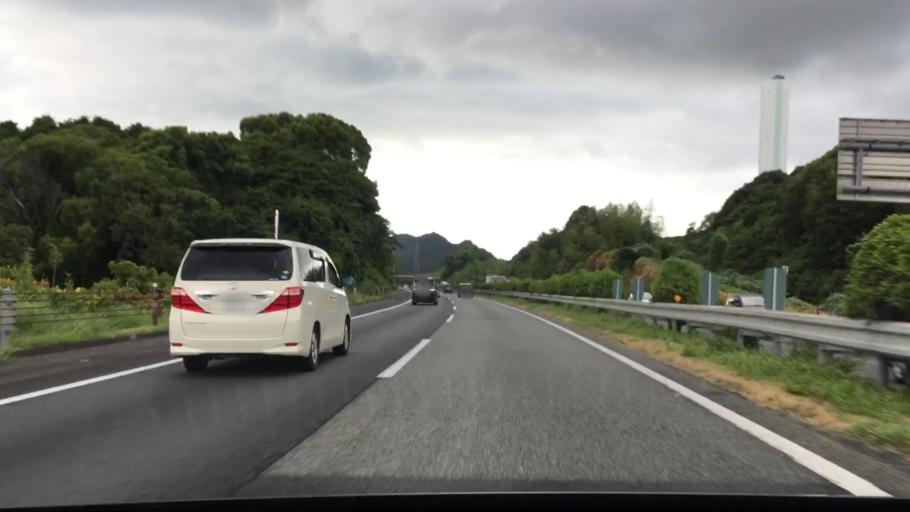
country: JP
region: Fukuoka
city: Sasaguri
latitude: 33.6398
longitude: 130.4885
